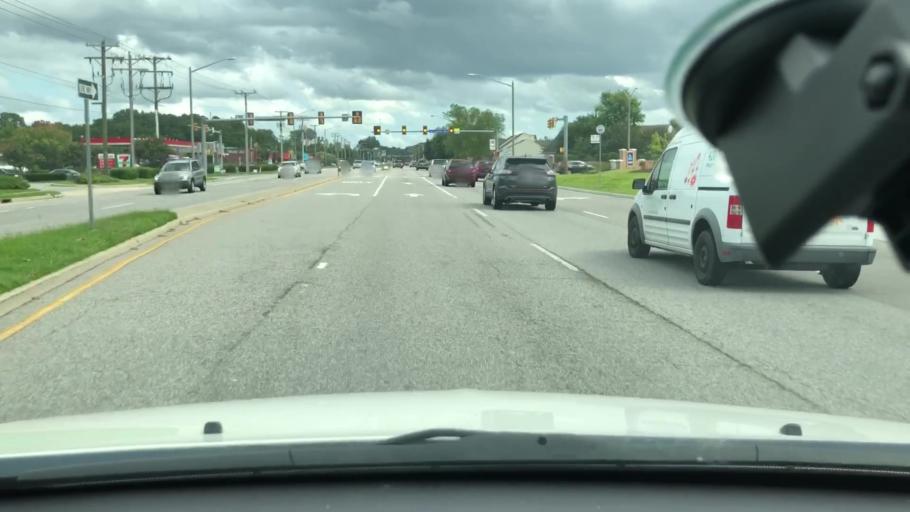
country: US
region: Virginia
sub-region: City of Chesapeake
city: Chesapeake
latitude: 36.7192
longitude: -76.2868
